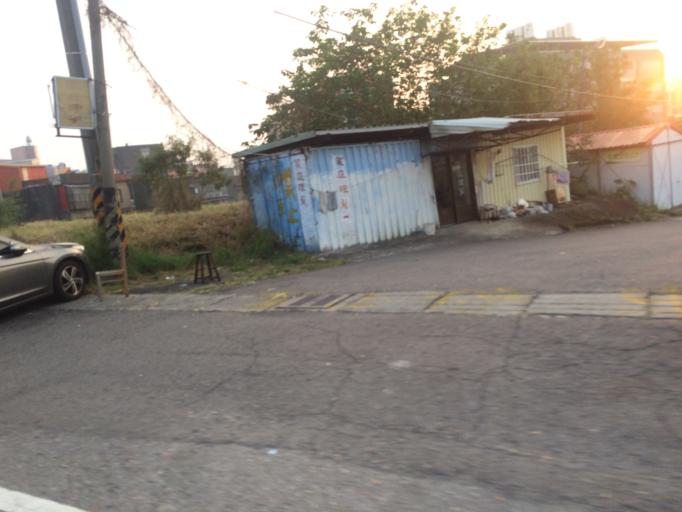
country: TW
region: Taiwan
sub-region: Hsinchu
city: Hsinchu
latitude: 24.7121
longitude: 120.9228
